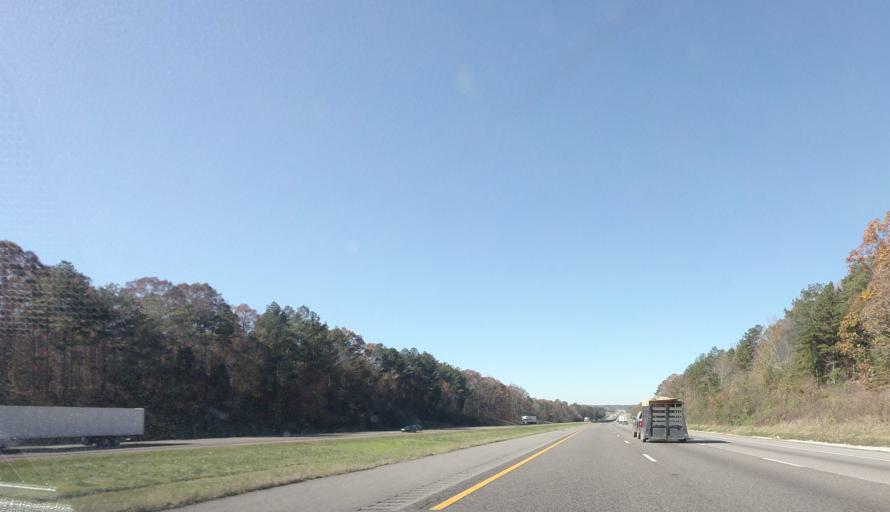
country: US
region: Alabama
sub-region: Calhoun County
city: Bynum
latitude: 33.5773
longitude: -86.0030
